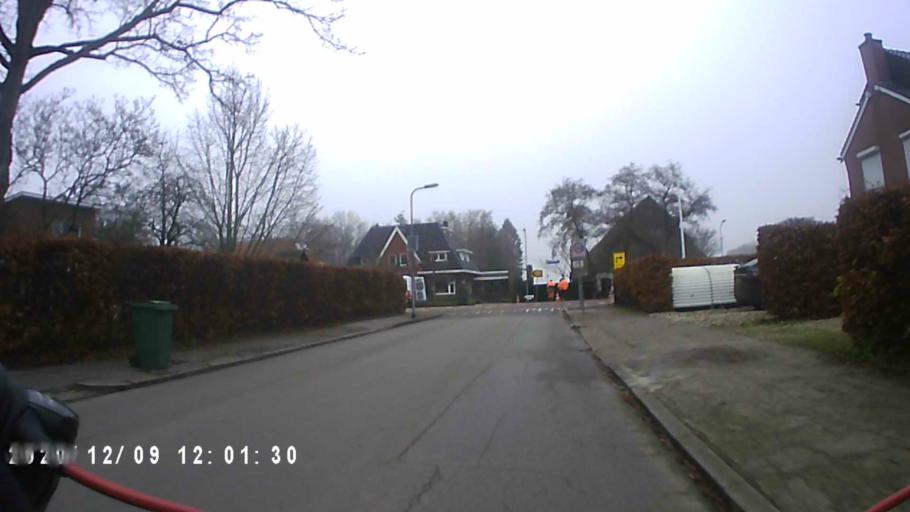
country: NL
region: Groningen
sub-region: Gemeente Haren
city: Haren
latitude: 53.1852
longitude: 6.6002
